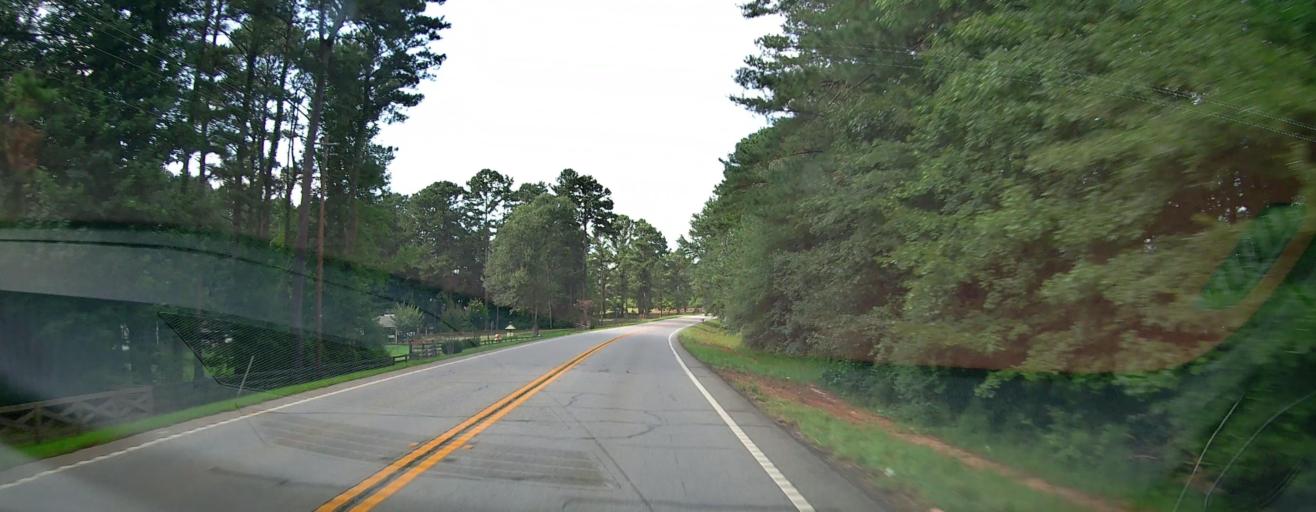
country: US
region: Georgia
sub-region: Coweta County
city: Senoia
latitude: 33.2110
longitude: -84.5803
